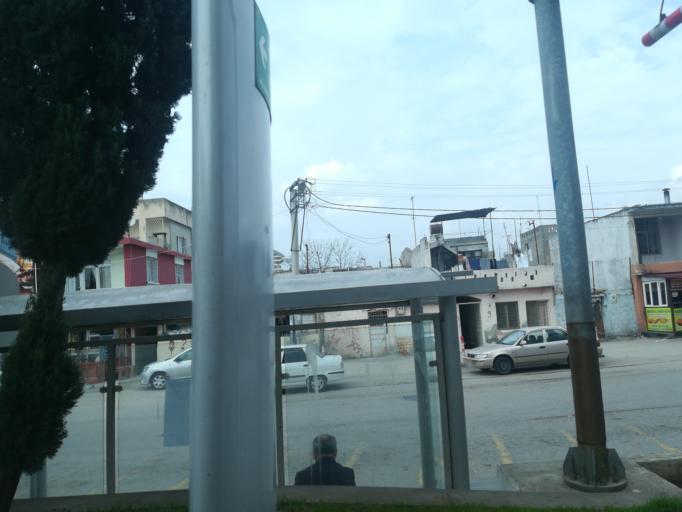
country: TR
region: Adana
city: Adana
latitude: 36.9917
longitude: 35.3394
